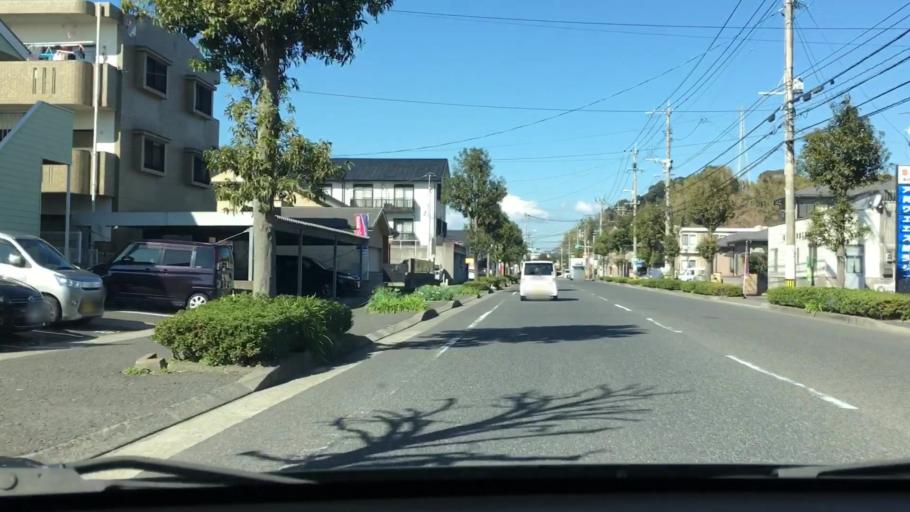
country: JP
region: Kagoshima
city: Kagoshima-shi
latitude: 31.5501
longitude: 130.5311
